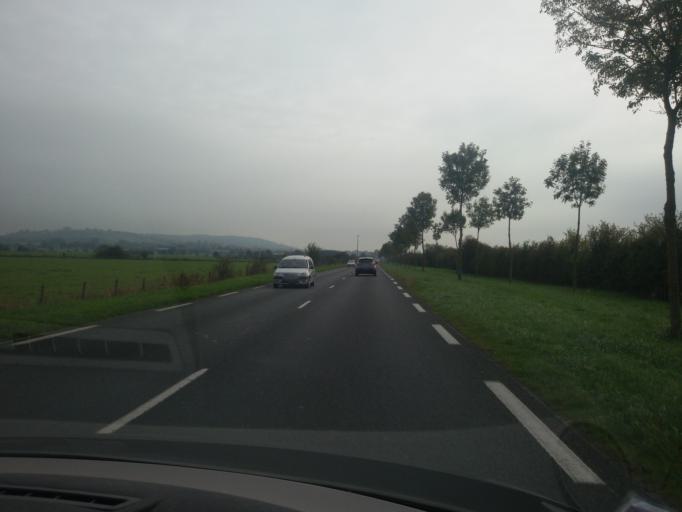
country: FR
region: Lower Normandy
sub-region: Departement du Calvados
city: Dives-sur-Mer
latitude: 49.2377
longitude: -0.0949
